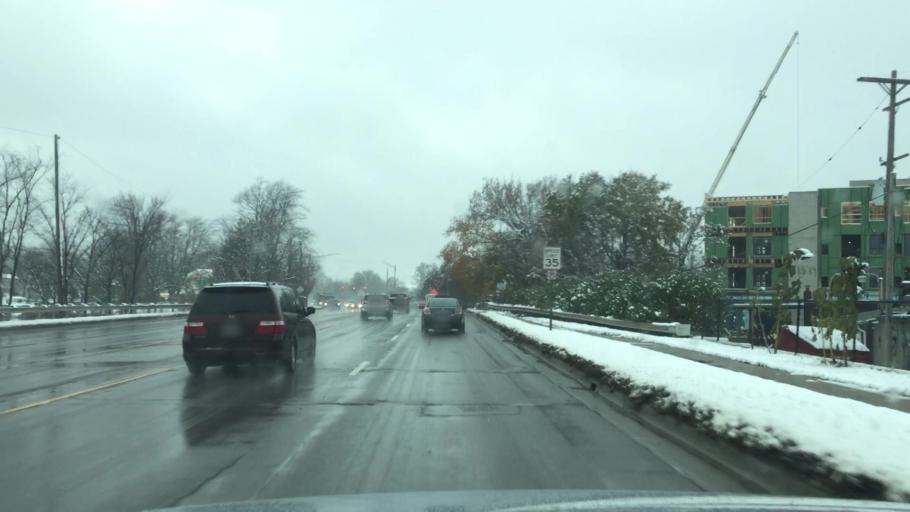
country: US
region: Michigan
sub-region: Oakland County
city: Lake Orion
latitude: 42.7824
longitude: -83.2400
